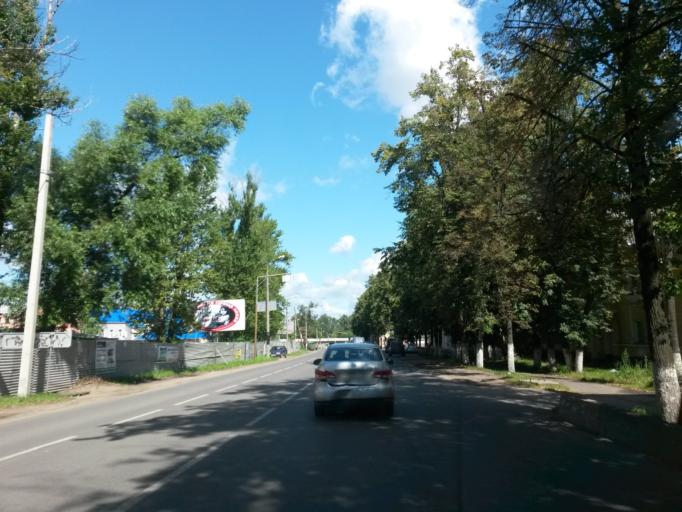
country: RU
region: Jaroslavl
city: Yaroslavl
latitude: 57.5994
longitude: 39.8781
